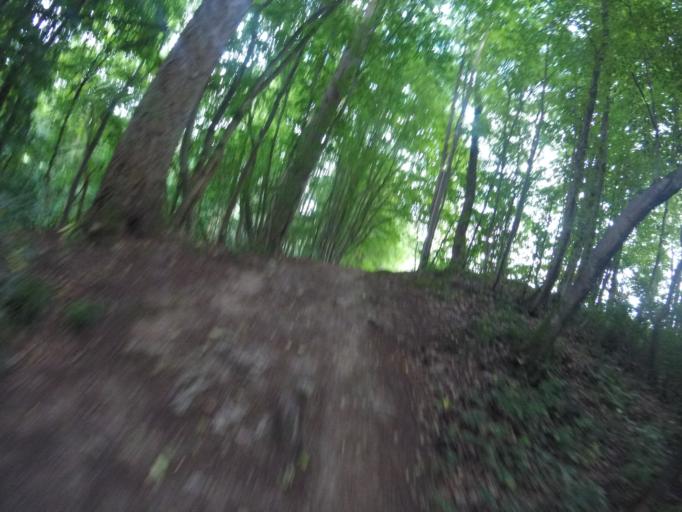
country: DE
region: Baden-Wuerttemberg
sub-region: Regierungsbezirk Stuttgart
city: Oppenweiler
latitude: 48.9645
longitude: 9.4639
